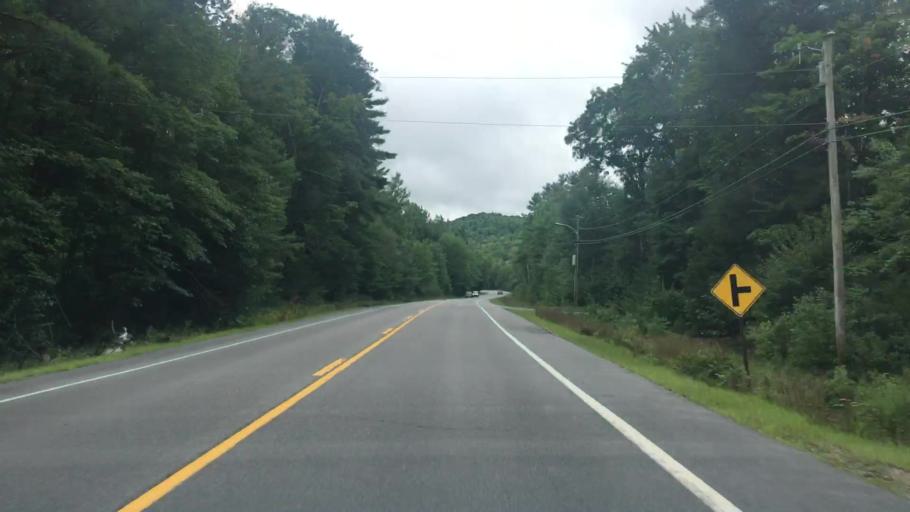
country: US
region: Maine
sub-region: York County
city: Cornish
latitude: 43.7836
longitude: -70.8231
